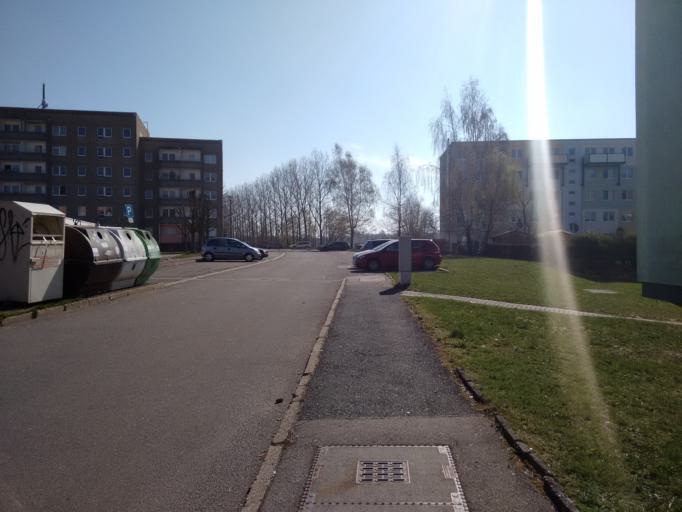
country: DE
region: Saxony
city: Limbach-Oberfrohna
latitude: 50.8529
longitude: 12.7630
